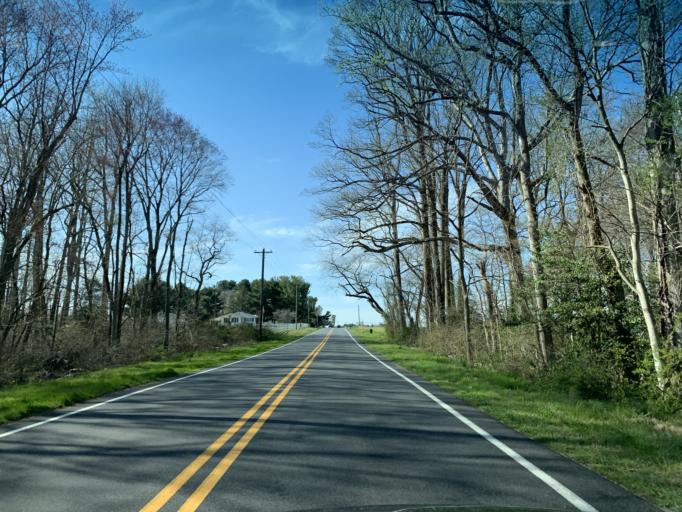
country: US
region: Delaware
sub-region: Kent County
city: Riverview
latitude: 39.0101
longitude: -75.5288
